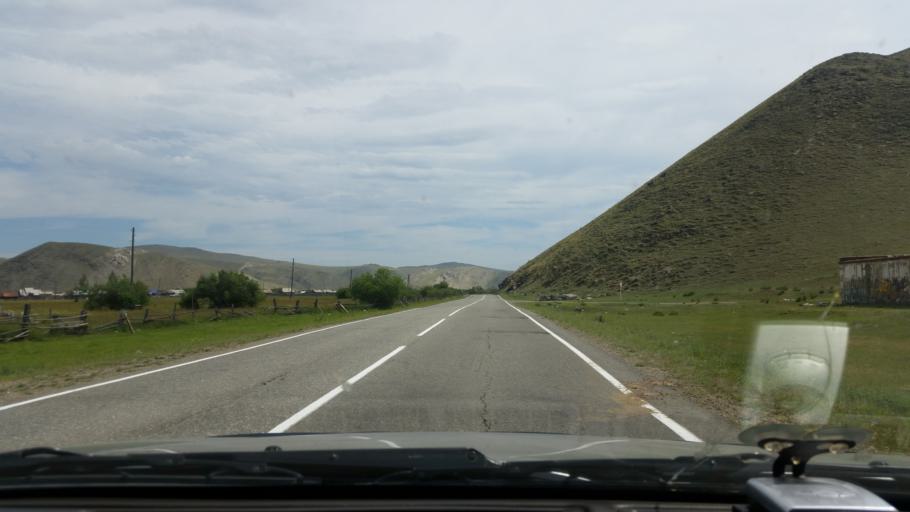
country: RU
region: Irkutsk
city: Yelantsy
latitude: 52.8064
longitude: 106.4592
